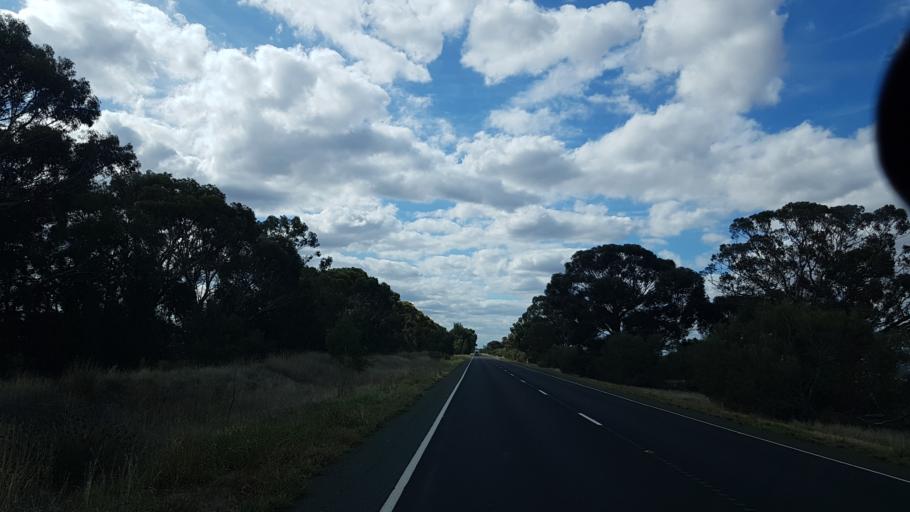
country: AU
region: Victoria
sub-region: Swan Hill
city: Swan Hill
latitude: -35.9812
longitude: 143.9450
